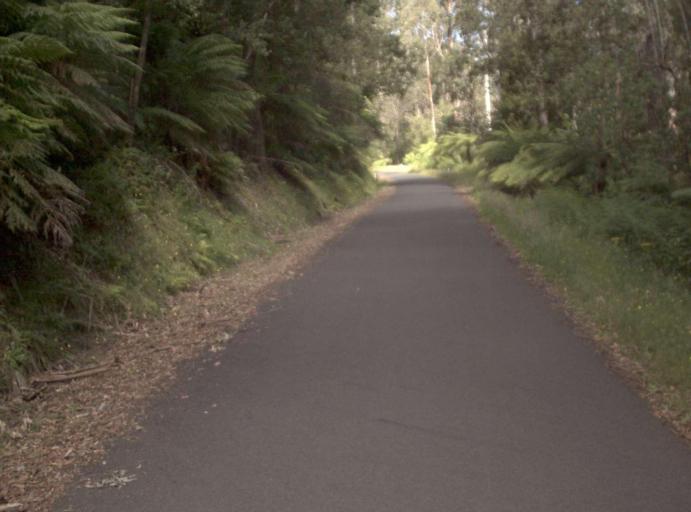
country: AU
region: Victoria
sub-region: Latrobe
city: Moe
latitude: -37.8395
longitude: 146.2110
